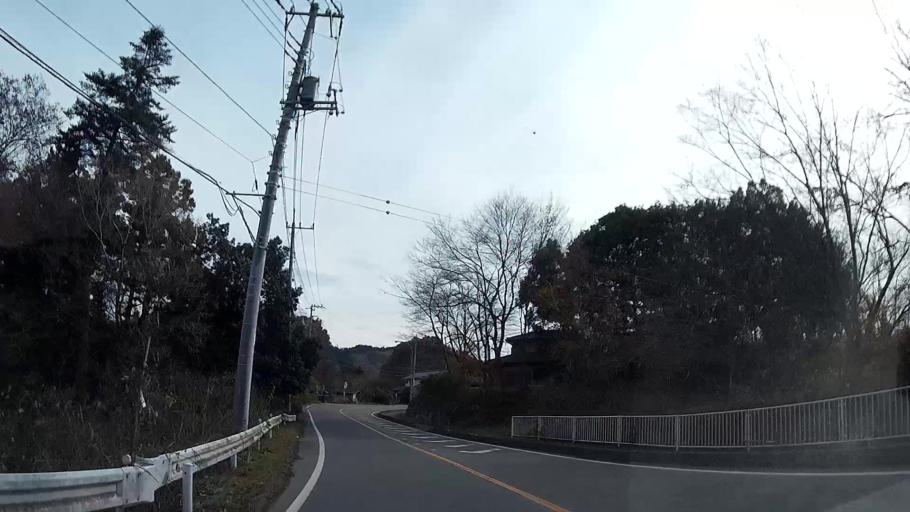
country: JP
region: Saitama
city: Chichibu
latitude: 36.0269
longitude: 139.0381
